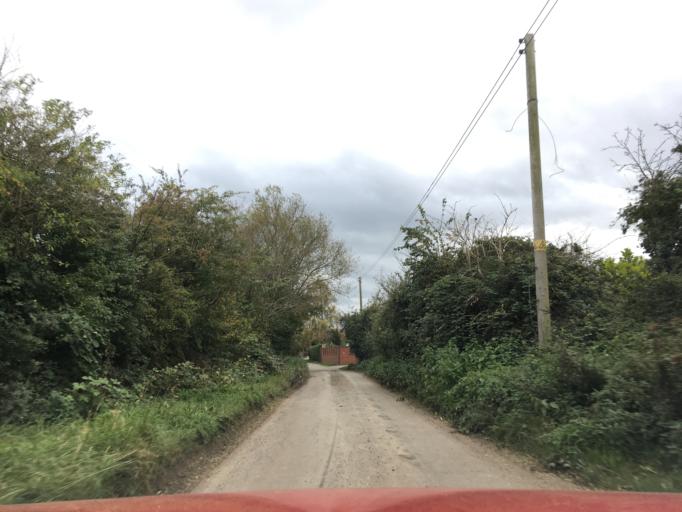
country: GB
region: England
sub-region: Gloucestershire
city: Stonehouse
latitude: 51.7622
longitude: -2.3062
